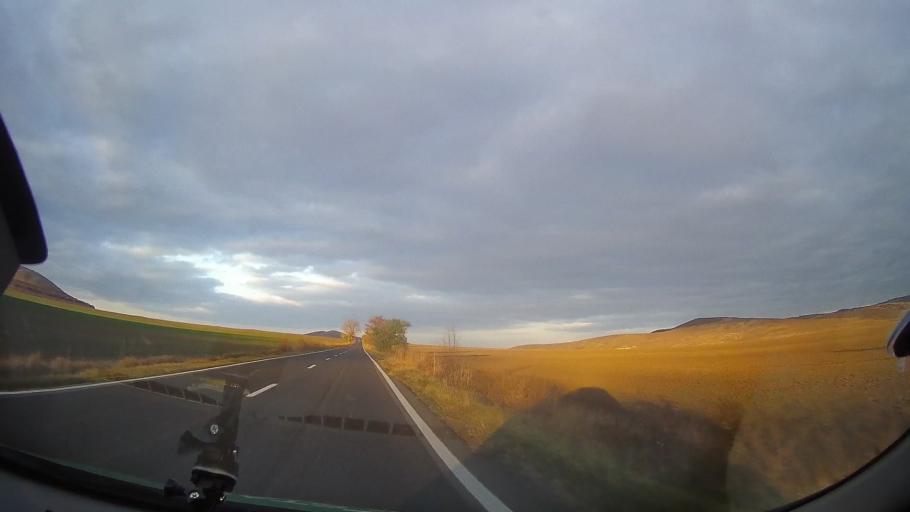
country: RO
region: Tulcea
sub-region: Comuna Nalbant
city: Nicolae Balcescu
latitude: 44.9749
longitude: 28.5435
